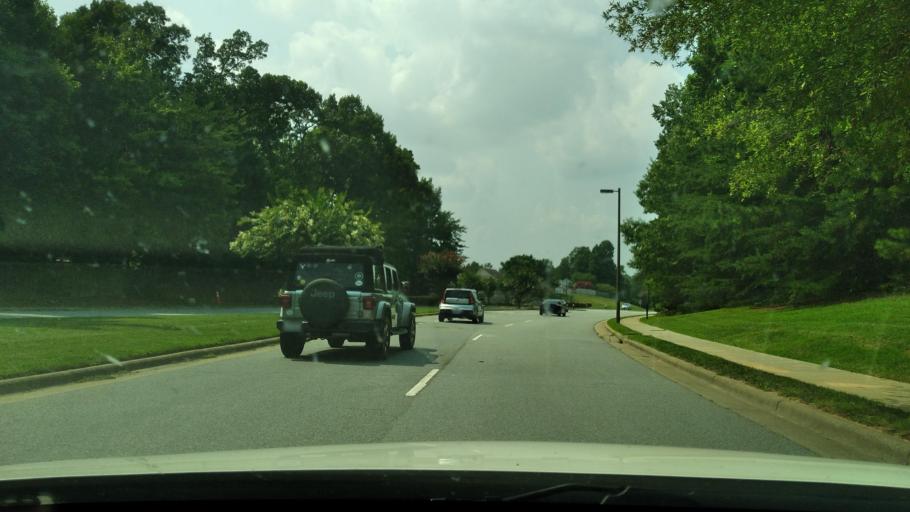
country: US
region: North Carolina
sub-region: Guilford County
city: Jamestown
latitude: 36.0402
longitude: -79.9226
